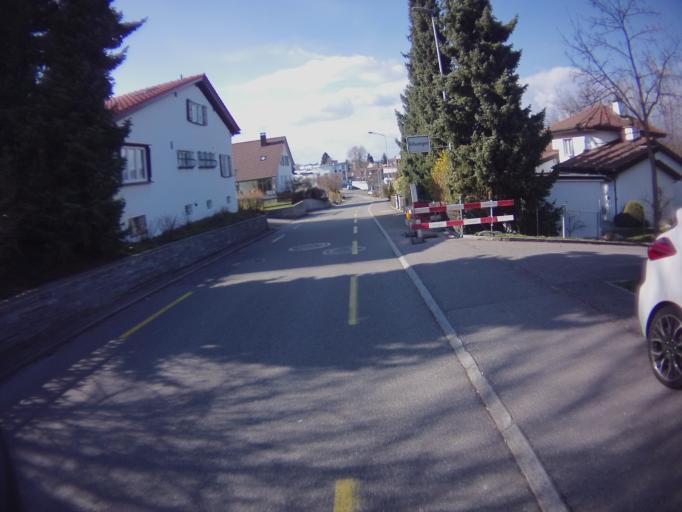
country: CH
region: Aargau
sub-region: Bezirk Baden
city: Killwangen
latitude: 47.4296
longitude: 8.3559
